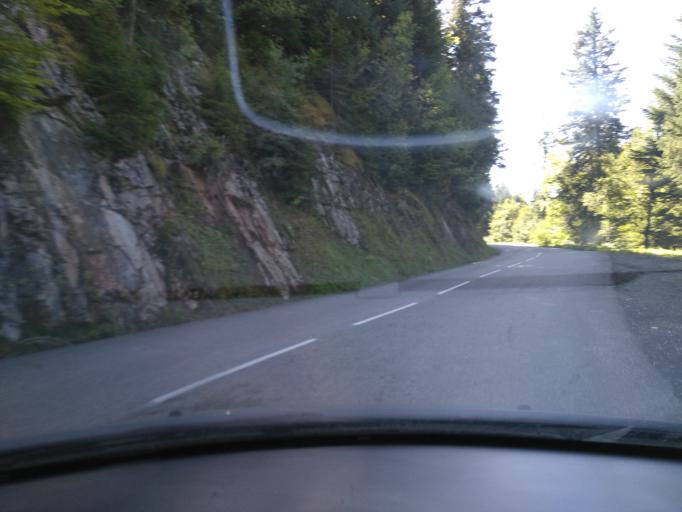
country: FR
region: Rhone-Alpes
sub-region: Departement de la Haute-Savoie
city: Praz-sur-Arly
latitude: 45.8031
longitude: 6.5038
